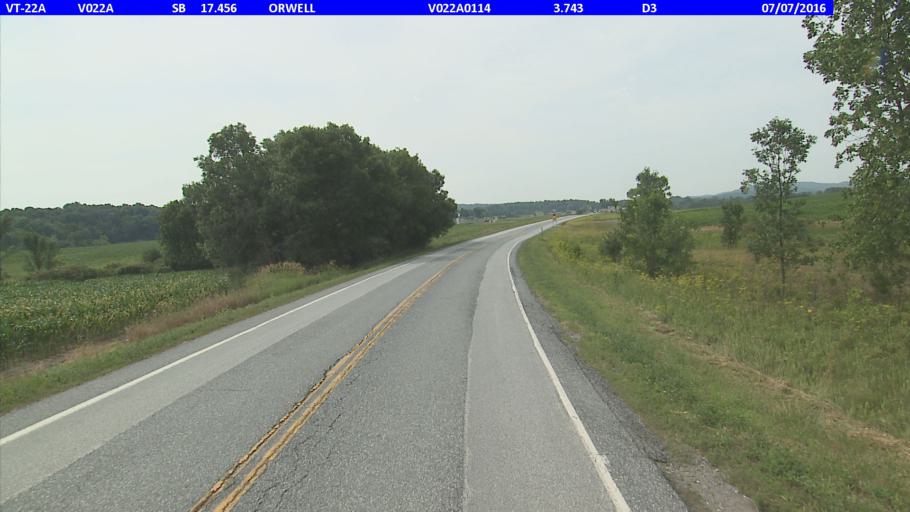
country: US
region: New York
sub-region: Essex County
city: Ticonderoga
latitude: 43.8109
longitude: -73.3041
